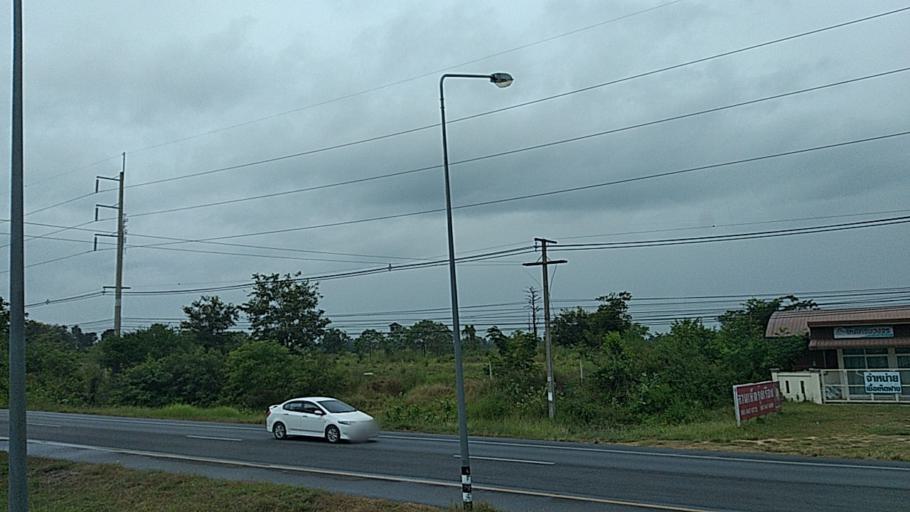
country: TH
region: Maha Sarakham
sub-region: Amphoe Borabue
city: Borabue
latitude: 16.0627
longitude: 103.1406
